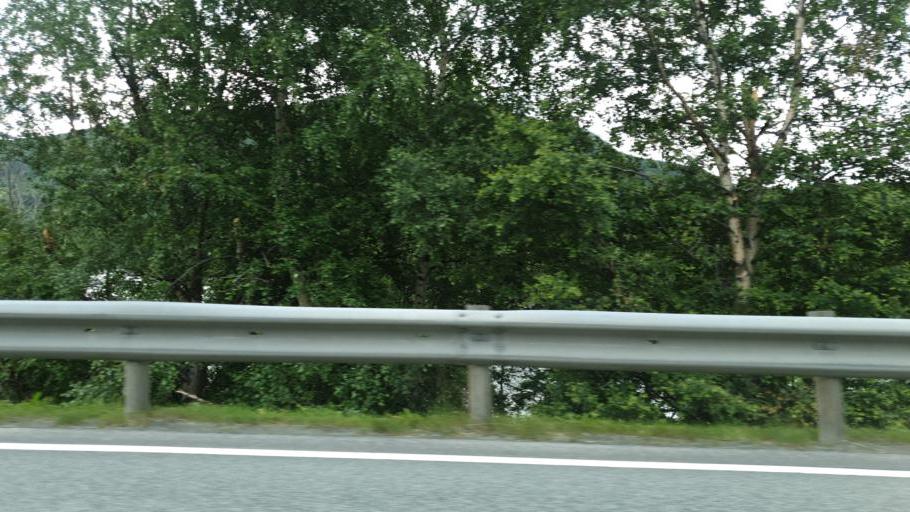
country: NO
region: Sor-Trondelag
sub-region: Oppdal
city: Oppdal
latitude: 62.5505
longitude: 9.6324
